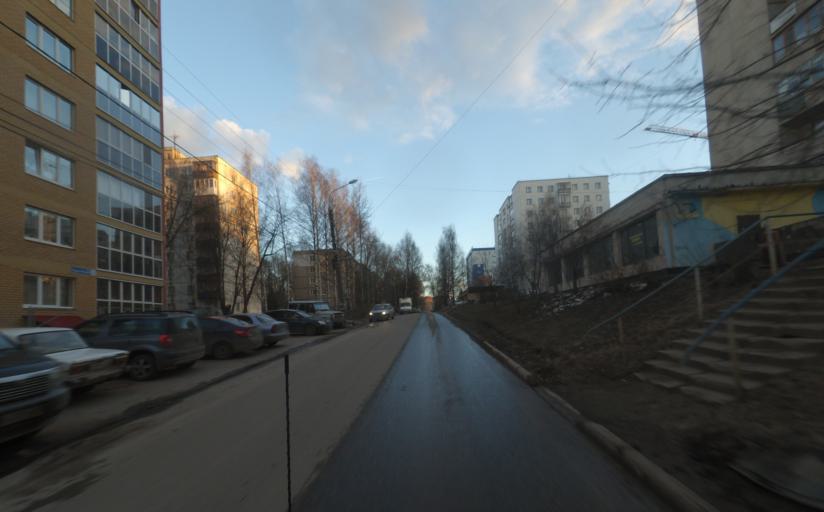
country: RU
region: Nizjnij Novgorod
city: Afonino
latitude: 56.2872
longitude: 44.0454
